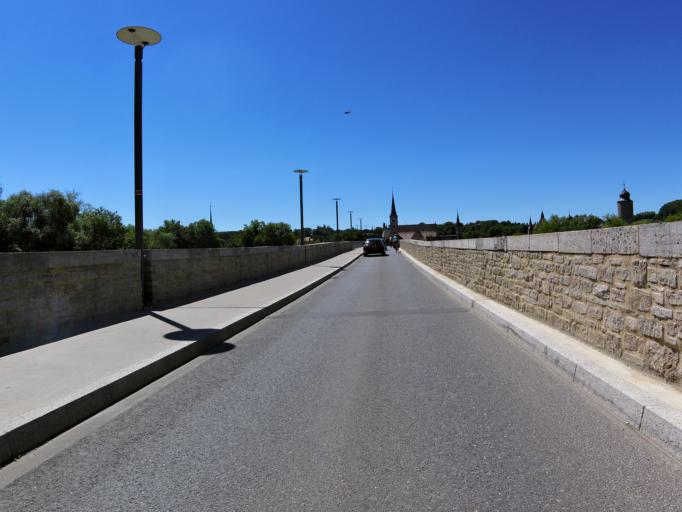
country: DE
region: Bavaria
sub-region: Regierungsbezirk Unterfranken
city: Ochsenfurt
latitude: 49.6681
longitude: 10.0634
